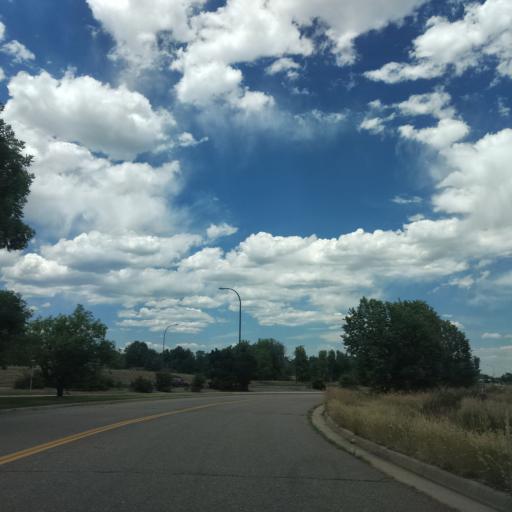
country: US
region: Colorado
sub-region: Jefferson County
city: Lakewood
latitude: 39.7052
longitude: -105.1091
